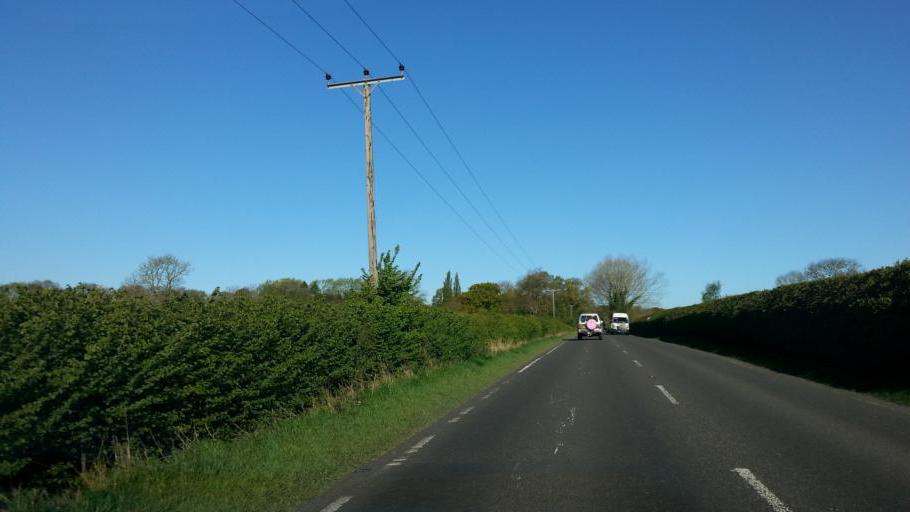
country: GB
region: England
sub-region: Nottinghamshire
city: Southwell
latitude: 53.1099
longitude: -0.9642
